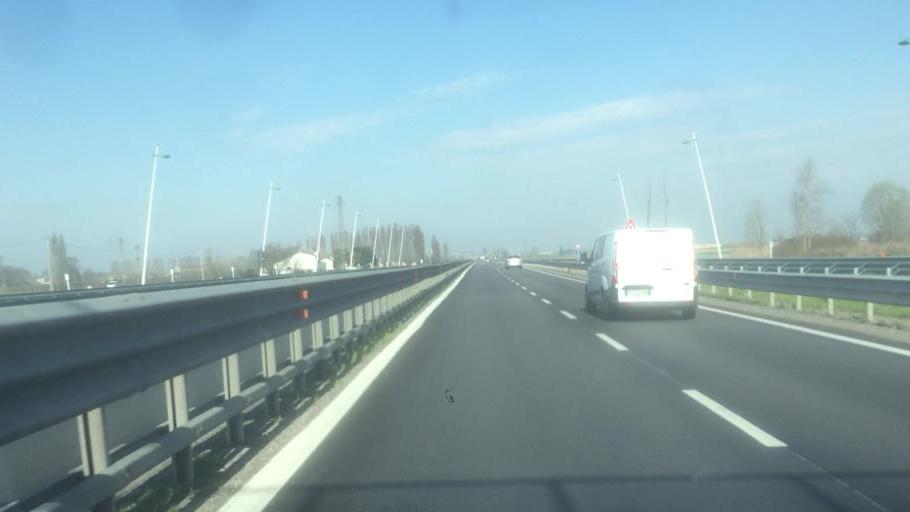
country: IT
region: Veneto
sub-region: Provincia di Rovigo
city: Canda
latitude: 45.0602
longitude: 11.5081
